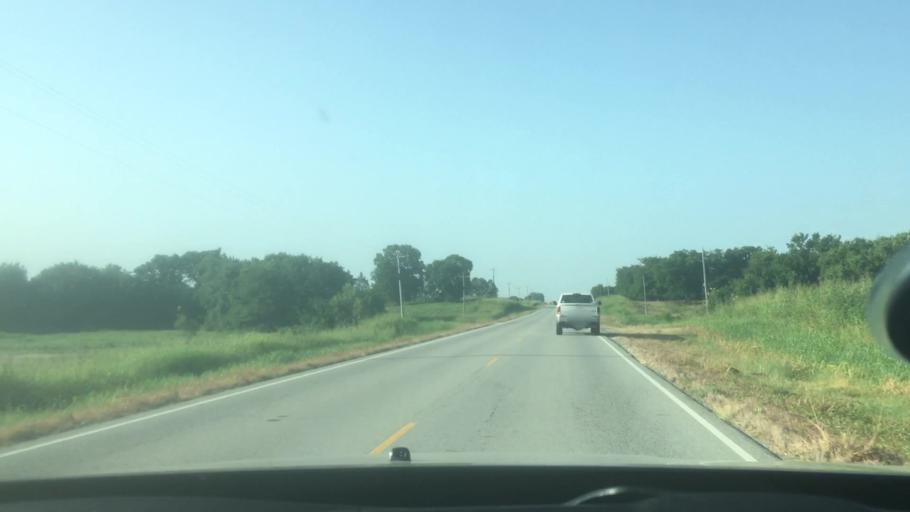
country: US
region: Oklahoma
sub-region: Coal County
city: Coalgate
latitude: 34.4593
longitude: -96.4246
